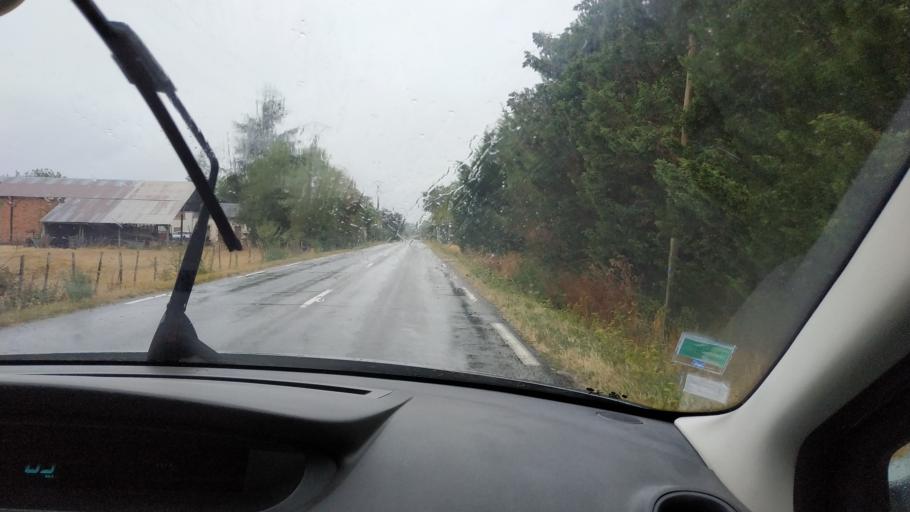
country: FR
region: Centre
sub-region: Departement du Loiret
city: Bellegarde
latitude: 47.9450
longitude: 2.3816
